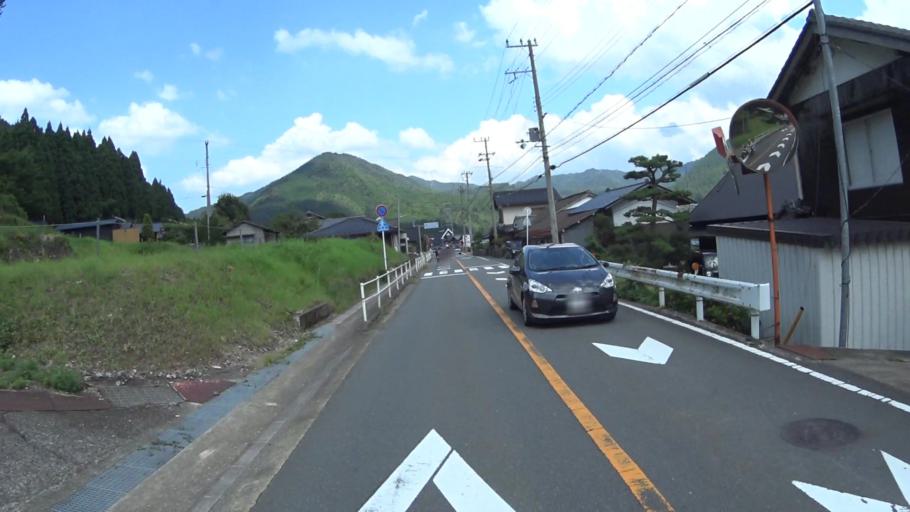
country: JP
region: Fukui
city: Obama
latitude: 35.2768
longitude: 135.5839
